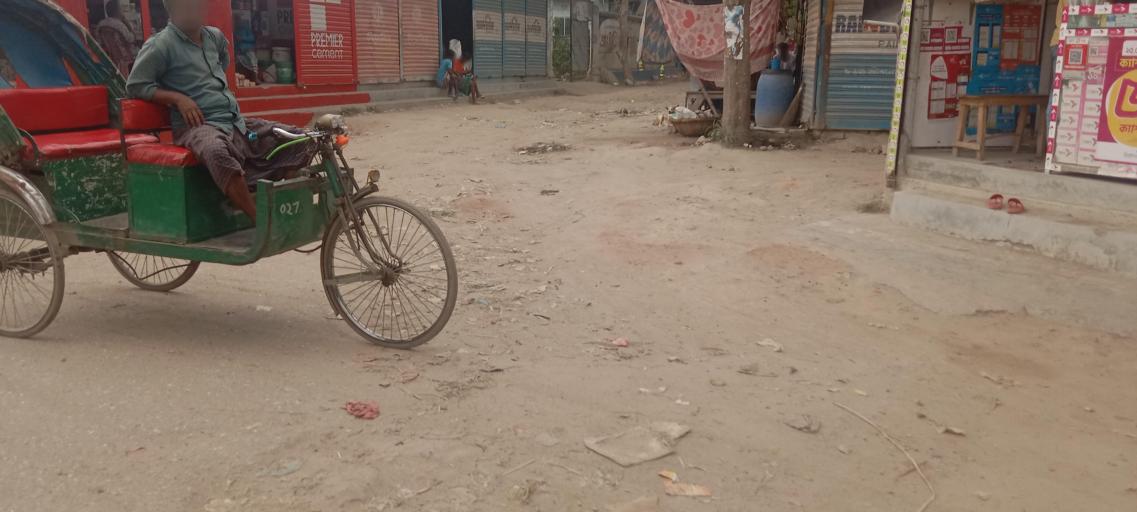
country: BD
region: Dhaka
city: Azimpur
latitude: 23.7059
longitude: 90.3585
